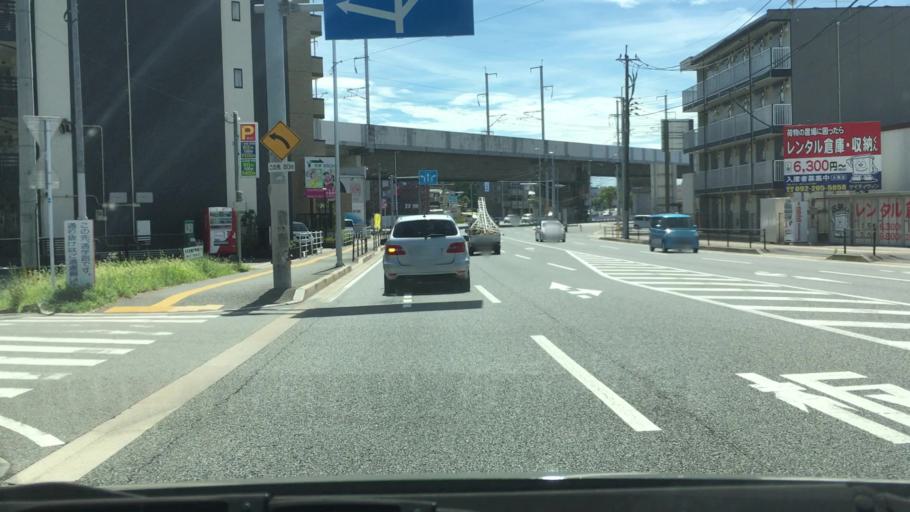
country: JP
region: Fukuoka
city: Fukuoka-shi
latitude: 33.5620
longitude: 130.4347
